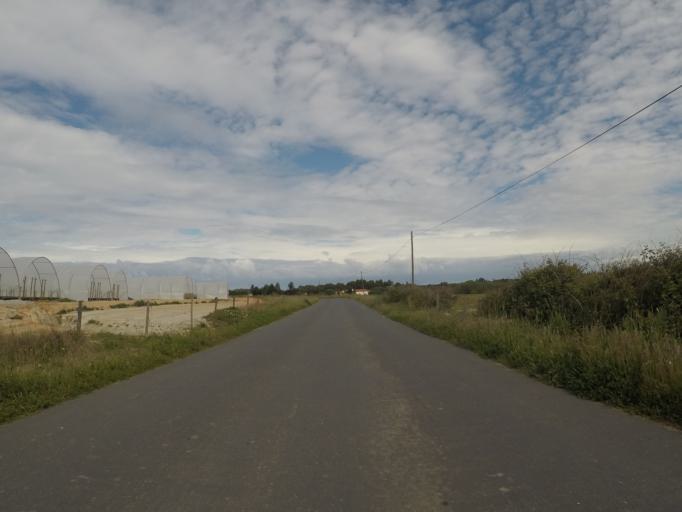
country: PT
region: Beja
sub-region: Odemira
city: Sao Teotonio
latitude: 37.4888
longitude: -8.7758
